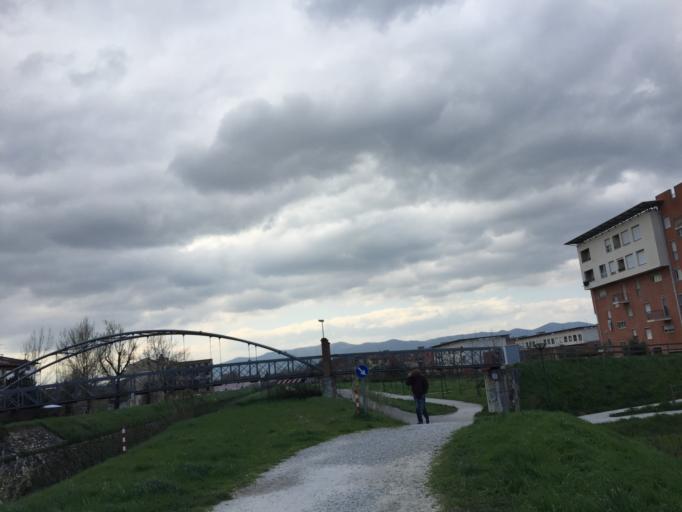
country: IT
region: Tuscany
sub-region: Provincia di Prato
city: Fornacelle
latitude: 43.8900
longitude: 11.0551
